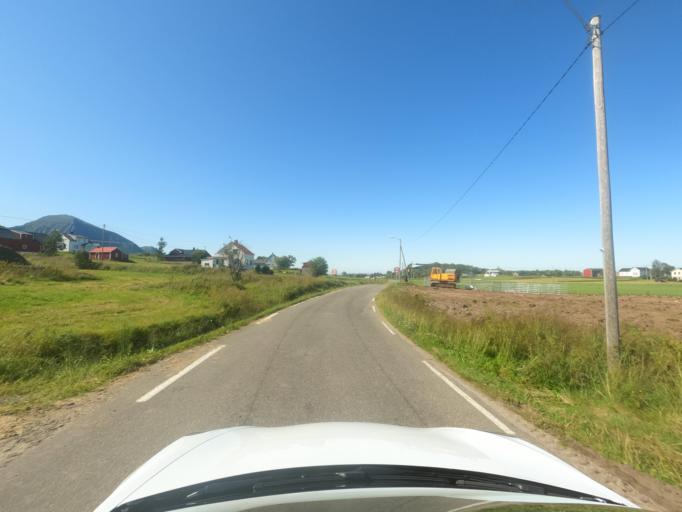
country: NO
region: Nordland
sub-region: Hadsel
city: Melbu
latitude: 68.4345
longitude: 14.7450
